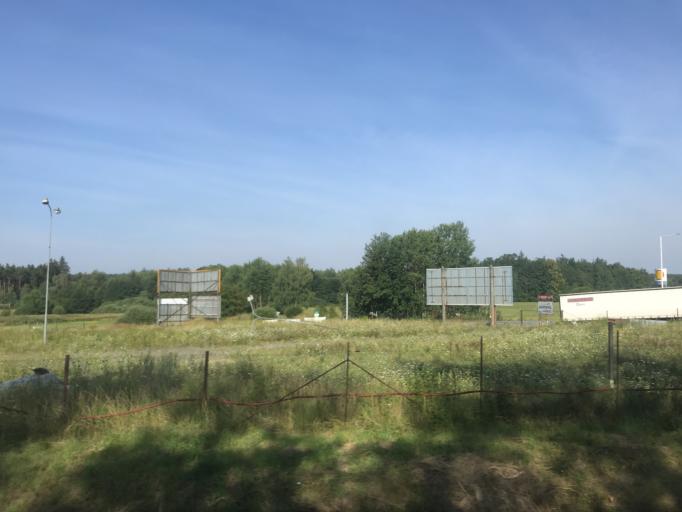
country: CZ
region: Jihocesky
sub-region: Okres Tabor
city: Sezimovo Usti
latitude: 49.3744
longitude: 14.6956
